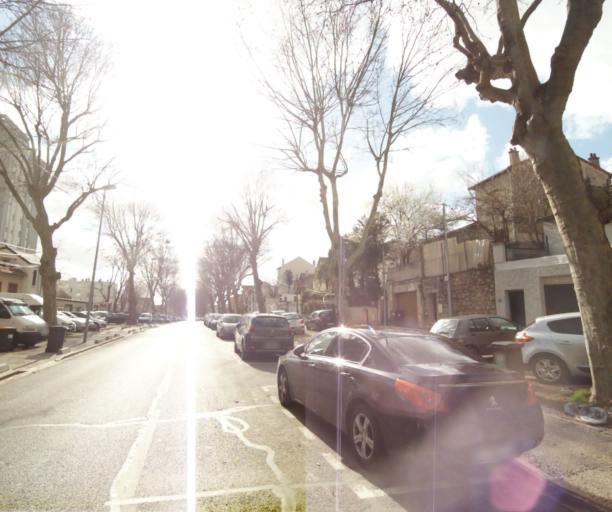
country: FR
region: Ile-de-France
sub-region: Departement de Seine-Saint-Denis
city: Pierrefitte-sur-Seine
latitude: 48.9715
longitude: 2.3644
